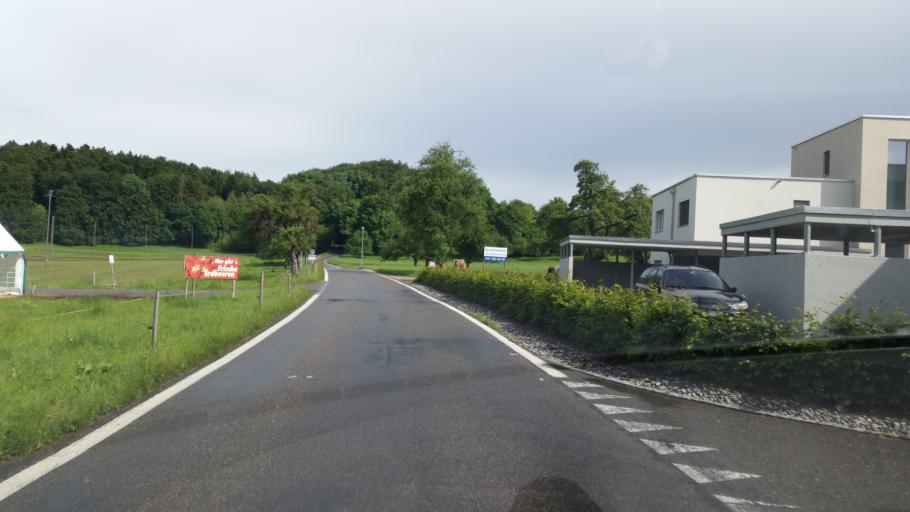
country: CH
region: Aargau
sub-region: Bezirk Lenzburg
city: Seengen
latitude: 47.3183
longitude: 8.2143
